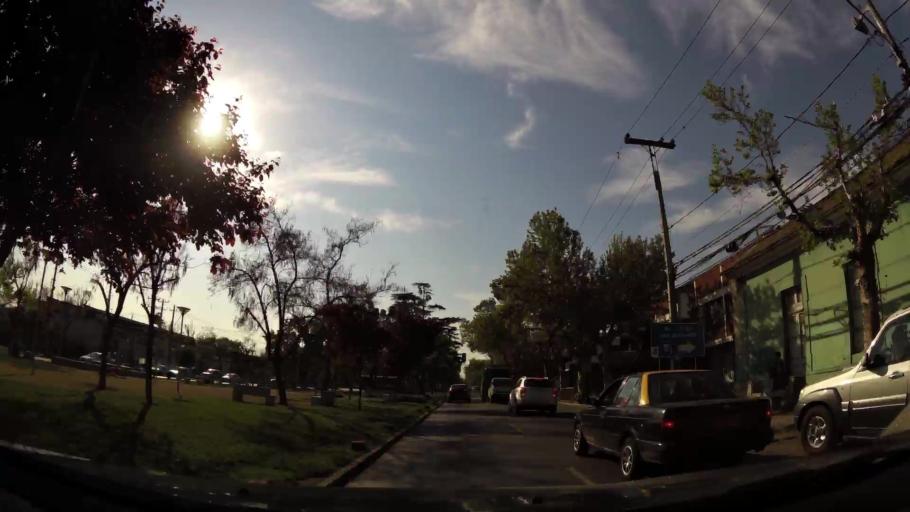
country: CL
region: Santiago Metropolitan
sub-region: Provincia de Maipo
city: San Bernardo
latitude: -33.5894
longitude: -70.7063
